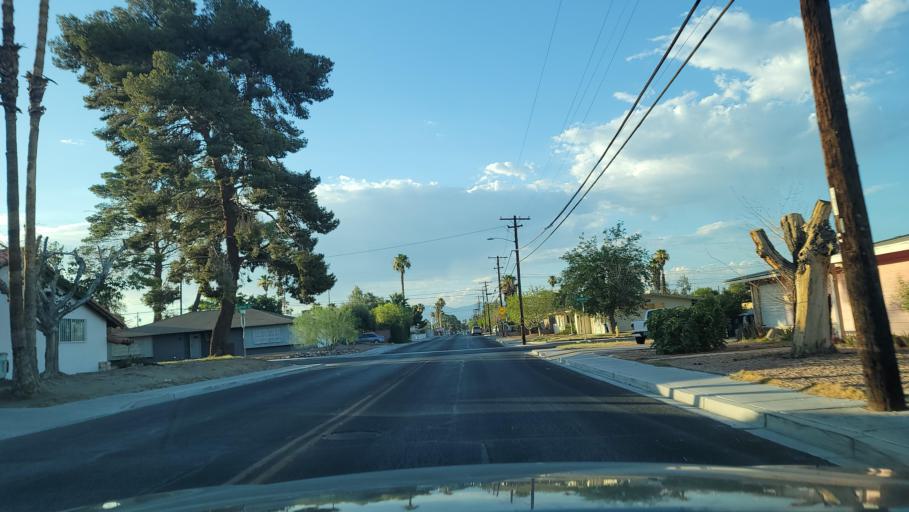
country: US
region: Nevada
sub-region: Clark County
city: Winchester
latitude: 36.1520
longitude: -115.1233
